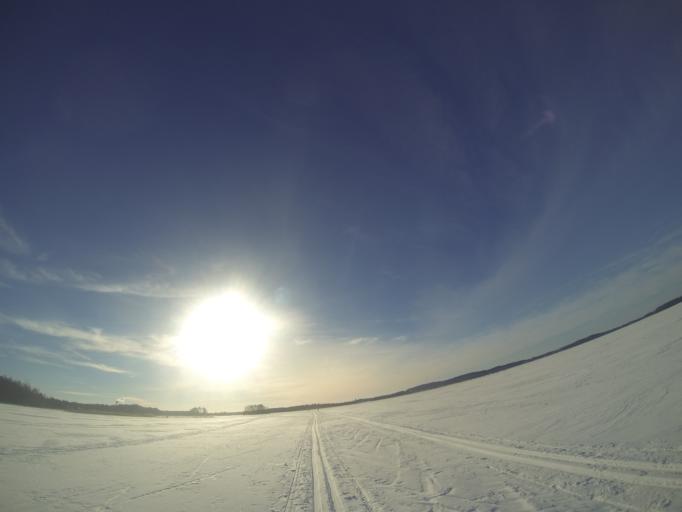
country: FI
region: Southern Savonia
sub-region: Savonlinna
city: Savonlinna
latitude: 61.8920
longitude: 28.9075
